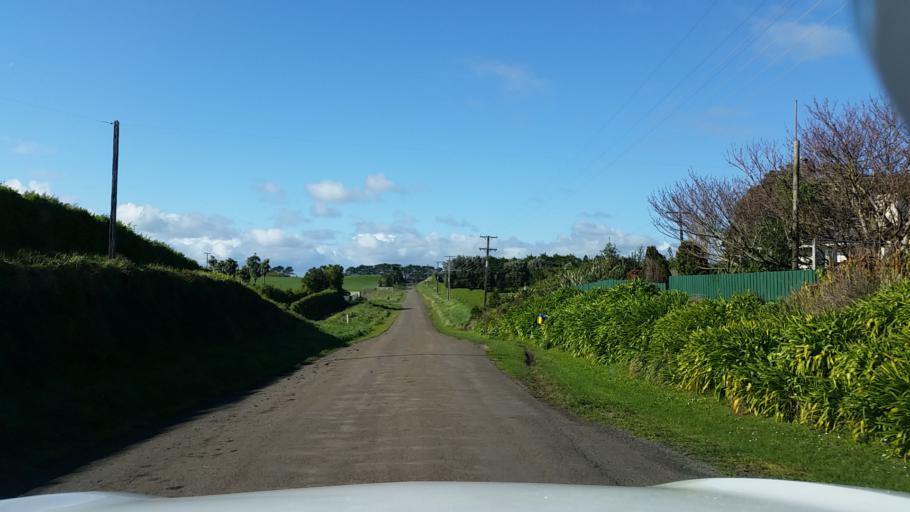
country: NZ
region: Taranaki
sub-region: South Taranaki District
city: Hawera
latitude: -39.6646
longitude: 174.3745
